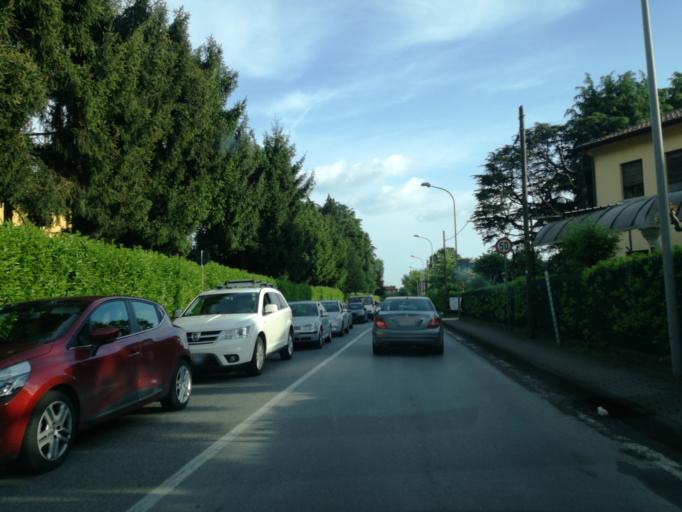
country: IT
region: Lombardy
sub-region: Provincia di Lecco
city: Paderno d'Adda
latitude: 45.6813
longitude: 9.4514
